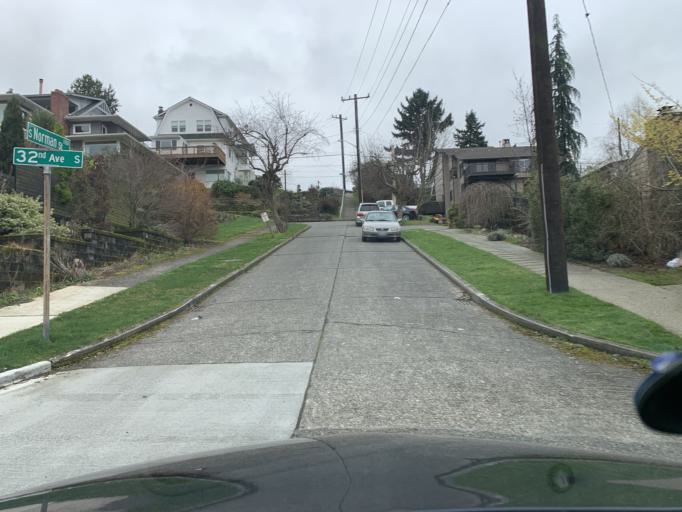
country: US
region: Washington
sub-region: King County
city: Seattle
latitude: 47.5935
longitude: -122.2916
